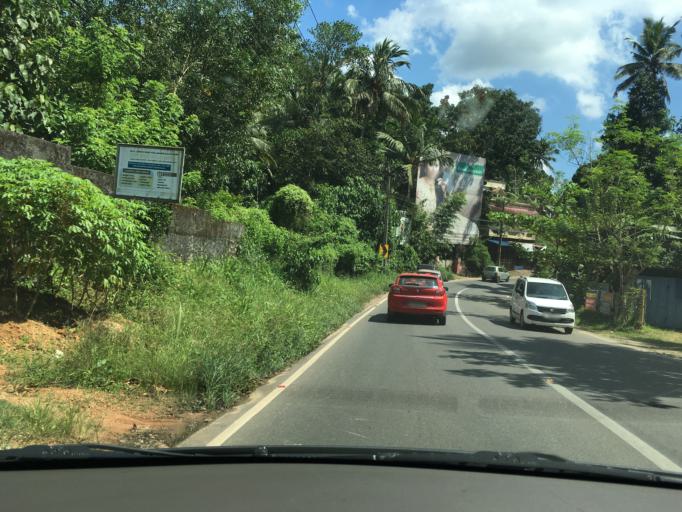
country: IN
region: Kerala
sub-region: Thiruvananthapuram
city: Nedumangad
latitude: 8.5795
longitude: 76.9961
